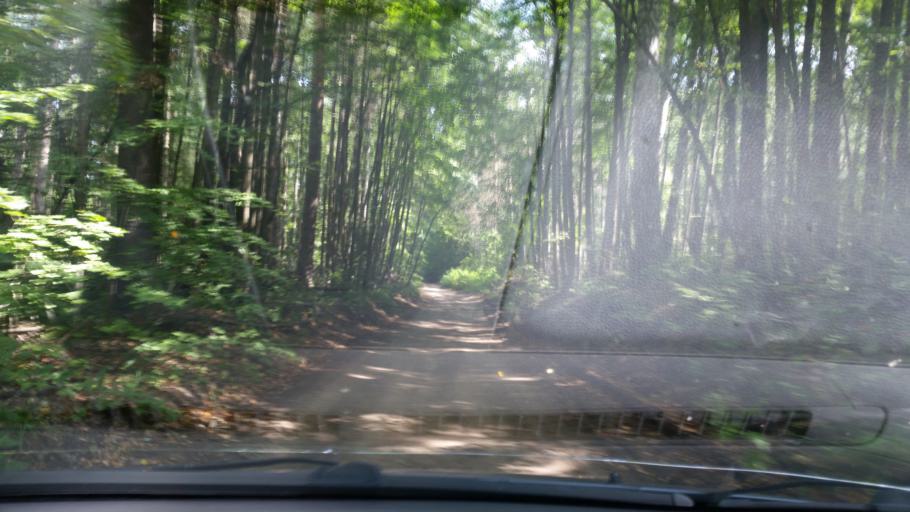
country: RU
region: Moskovskaya
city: Pushchino
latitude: 54.9127
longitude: 37.7194
